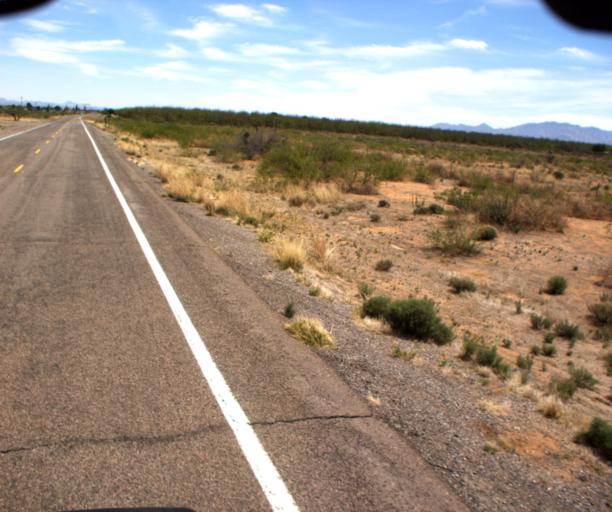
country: US
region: Arizona
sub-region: Cochise County
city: Willcox
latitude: 32.3298
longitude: -109.5042
